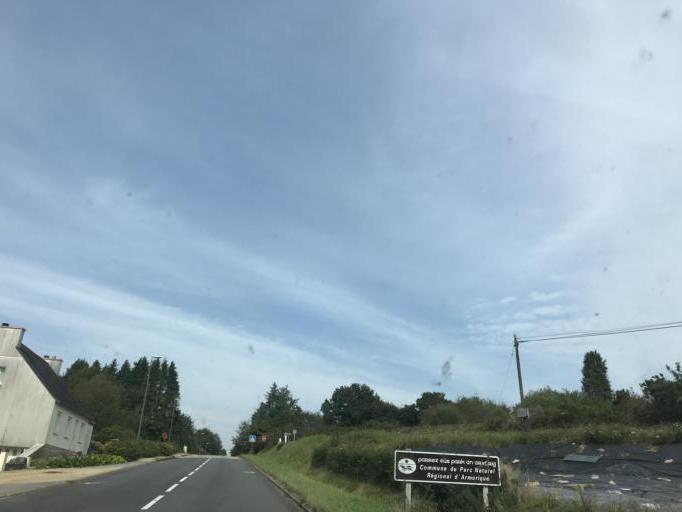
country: FR
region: Brittany
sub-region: Departement du Finistere
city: Plouneour-Menez
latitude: 48.3565
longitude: -3.8534
